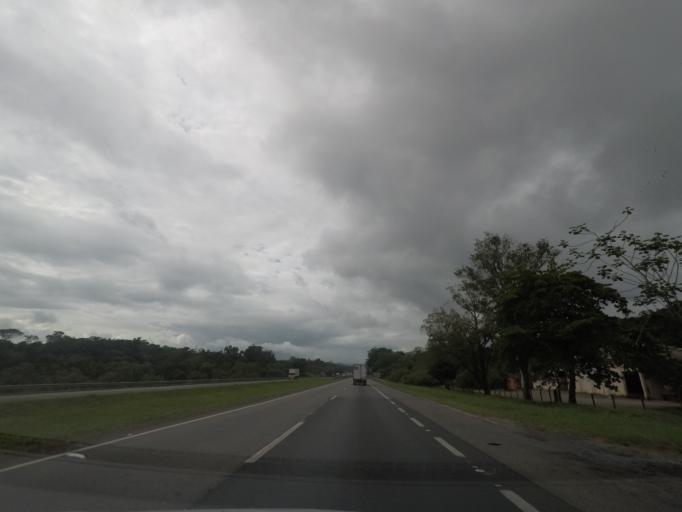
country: BR
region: Sao Paulo
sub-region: Miracatu
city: Miracatu
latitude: -24.2775
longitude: -47.4176
